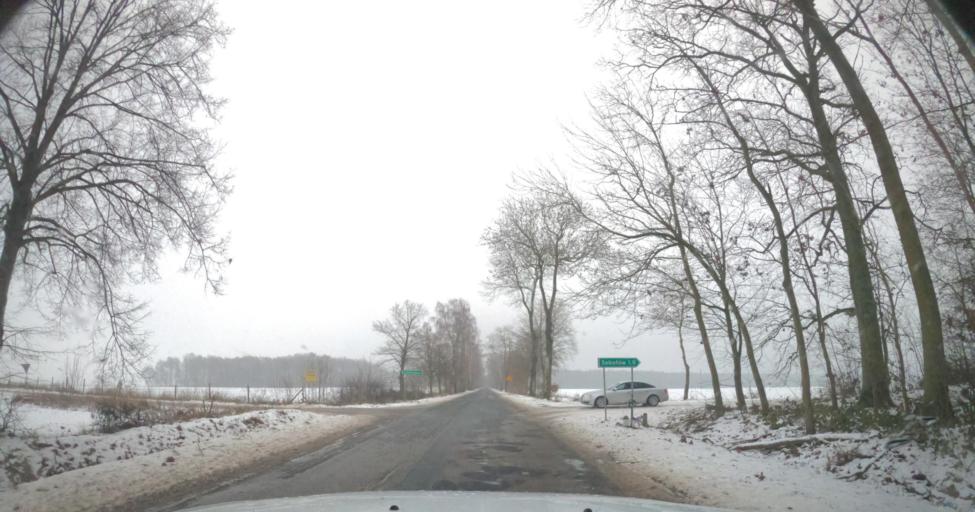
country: PL
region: West Pomeranian Voivodeship
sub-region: Powiat gryficki
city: Gryfice
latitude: 53.9086
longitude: 15.2488
